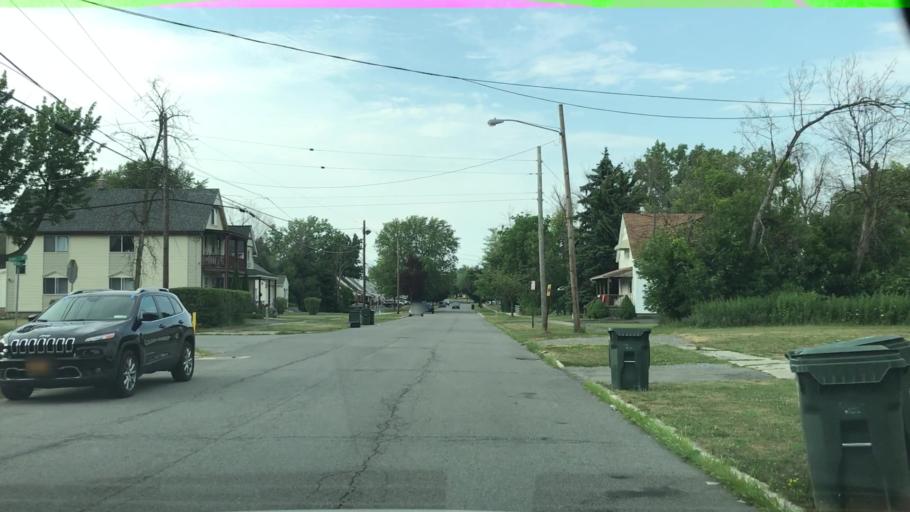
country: US
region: New York
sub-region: Erie County
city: Depew
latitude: 42.9136
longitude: -78.6926
